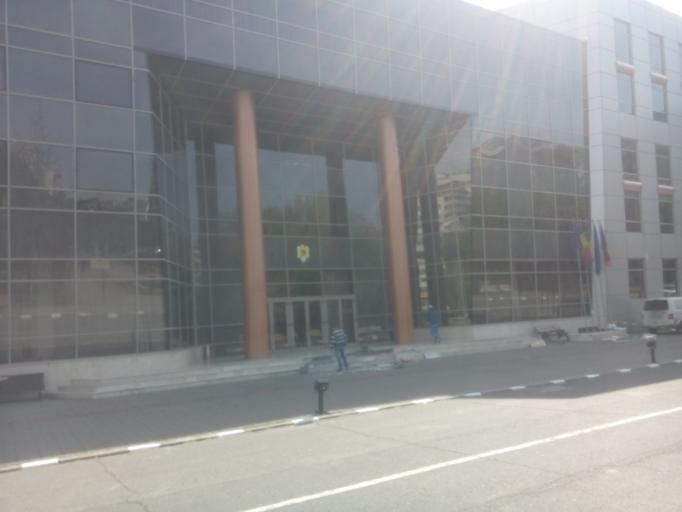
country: RO
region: Bucuresti
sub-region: Municipiul Bucuresti
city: Bucharest
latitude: 44.4487
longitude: 26.1272
